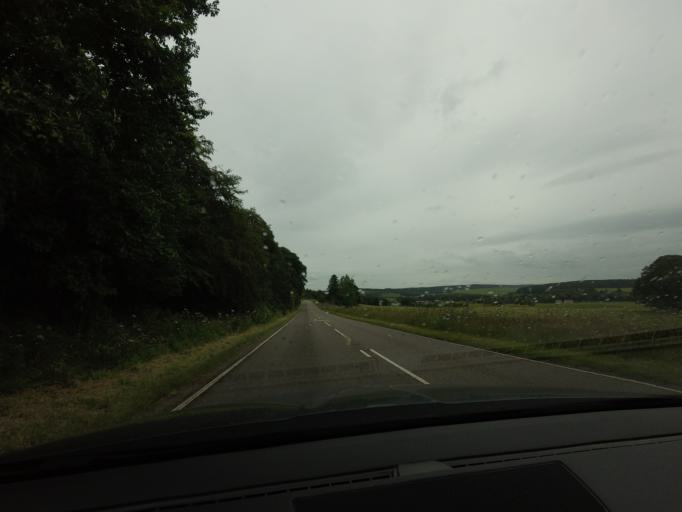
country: GB
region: Scotland
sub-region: Moray
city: Cullen
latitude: 57.6827
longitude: -2.8097
